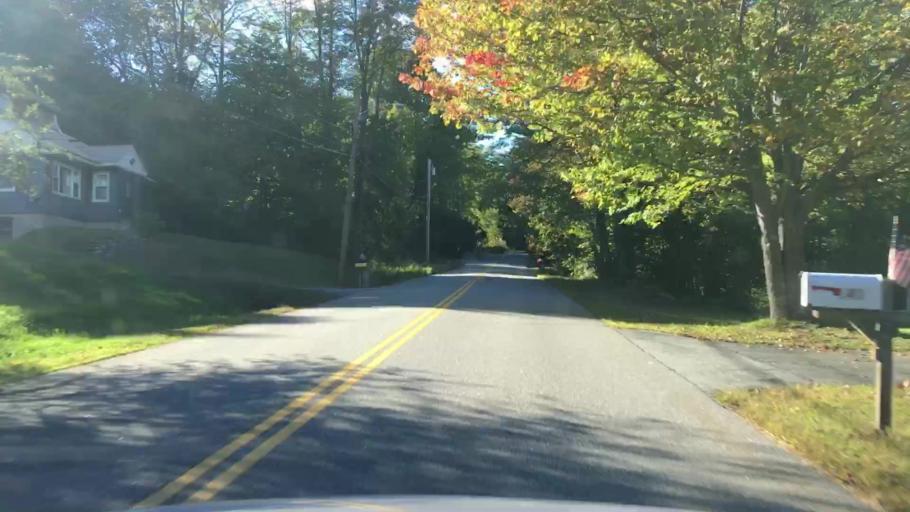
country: US
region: Maine
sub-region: Androscoggin County
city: Sabattus
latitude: 44.0775
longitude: -70.1497
